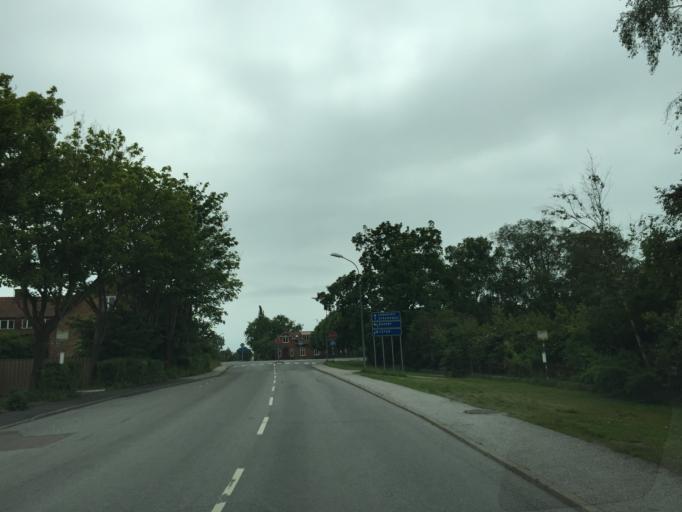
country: SE
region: Skane
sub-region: Ystads Kommun
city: Kopingebro
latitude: 55.4294
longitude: 14.1130
